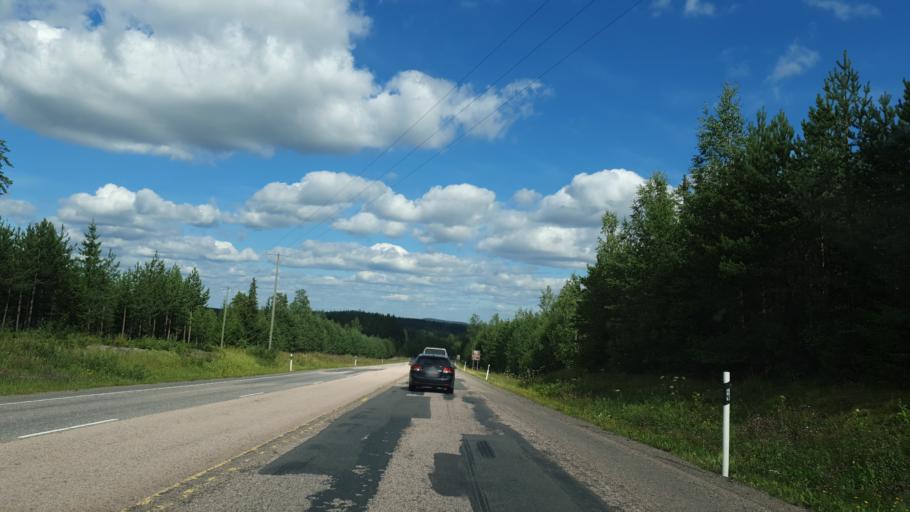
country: FI
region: Central Finland
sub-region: Jaemsae
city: Jaemsae
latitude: 61.8290
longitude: 25.0832
